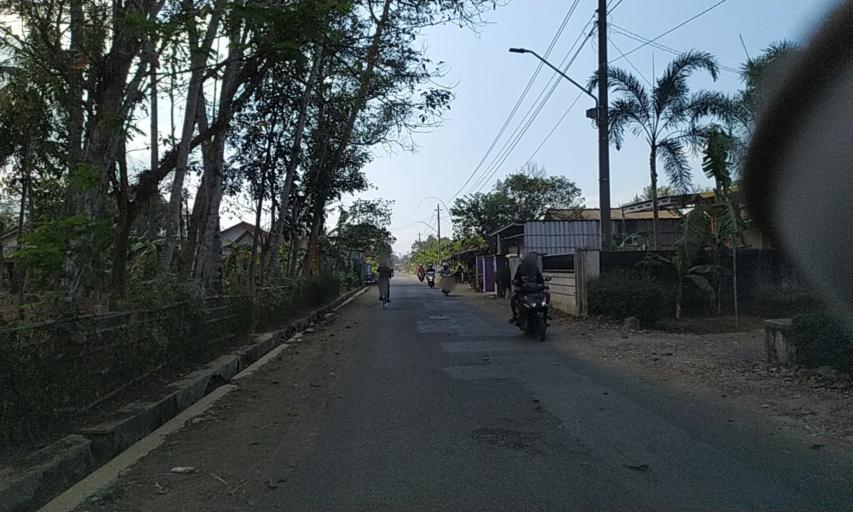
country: ID
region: Central Java
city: Adipala
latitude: -7.6650
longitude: 109.1643
